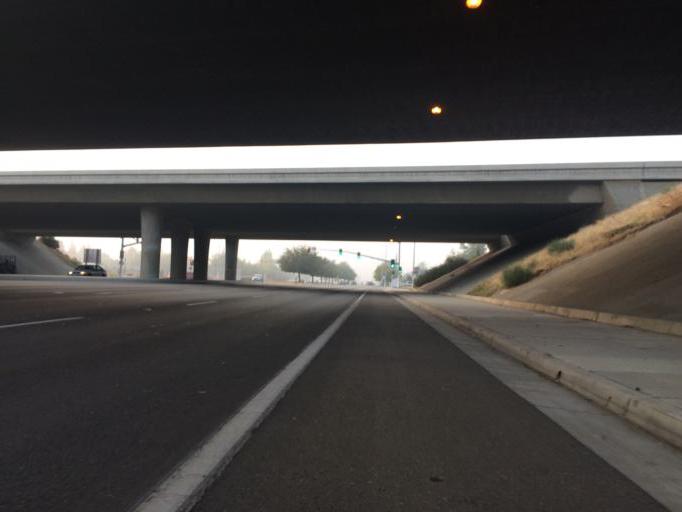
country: US
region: California
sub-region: Fresno County
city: Fresno
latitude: 36.7551
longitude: -119.7365
